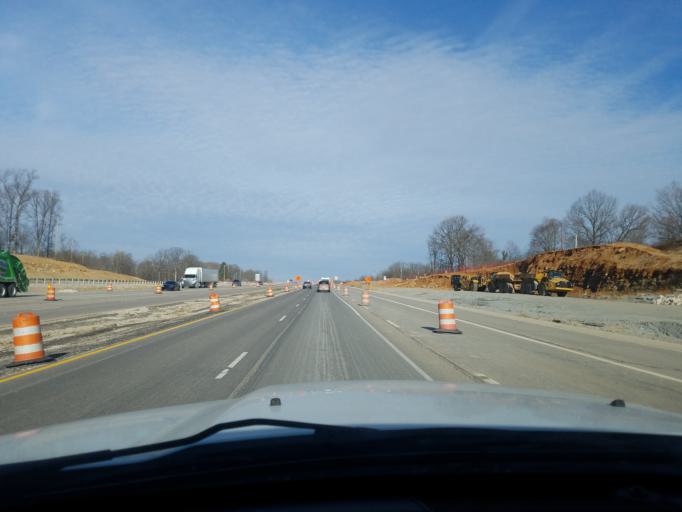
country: US
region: Indiana
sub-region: Monroe County
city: Bloomington
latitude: 39.2500
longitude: -86.5308
